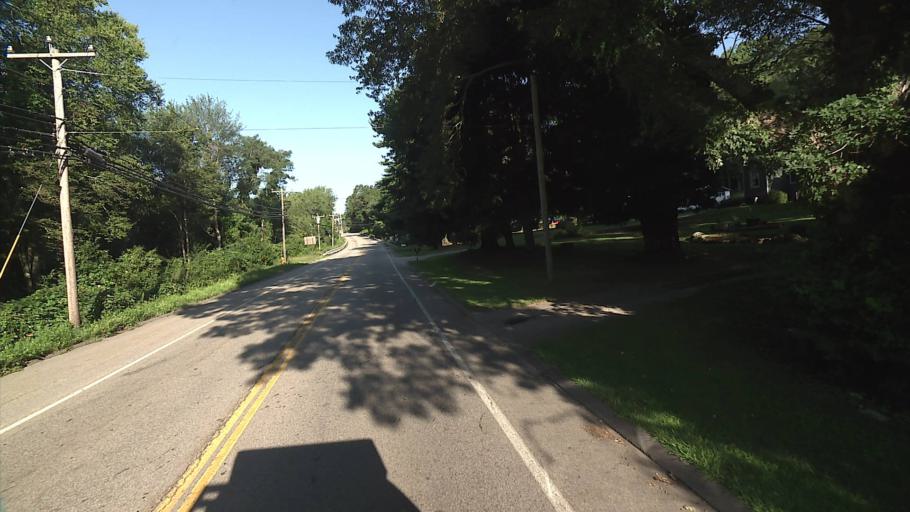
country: US
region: Connecticut
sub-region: New London County
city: Central Waterford
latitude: 41.3514
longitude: -72.1562
